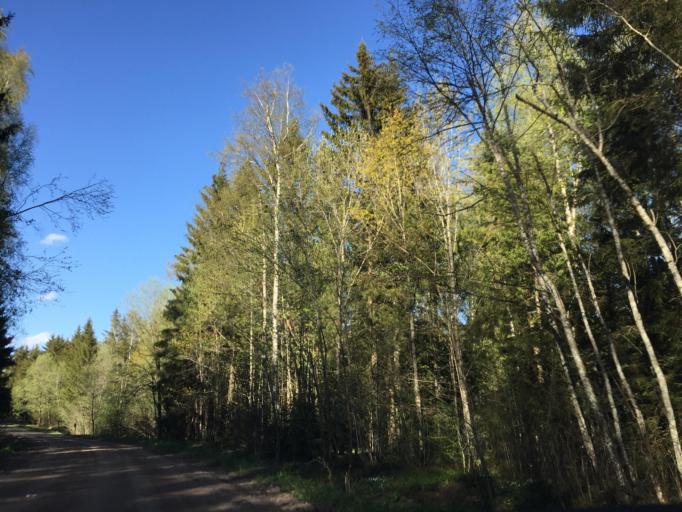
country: LV
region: Vecpiebalga
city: Vecpiebalga
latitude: 56.8587
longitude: 25.9632
